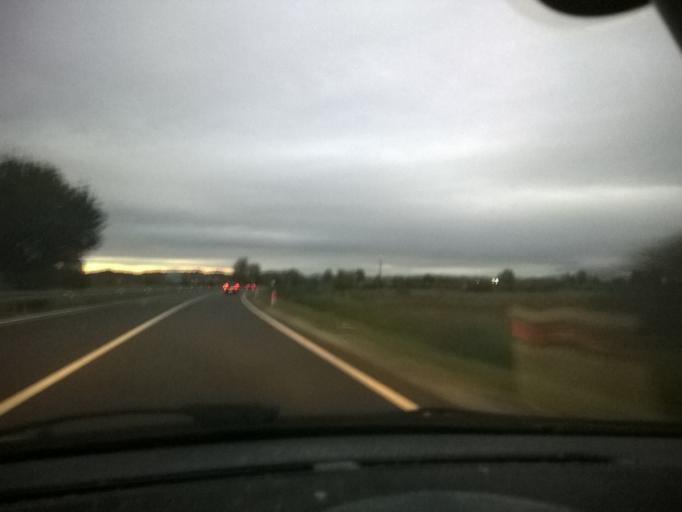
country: HR
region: Zagrebacka
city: Jakovlje
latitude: 45.9837
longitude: 15.8457
